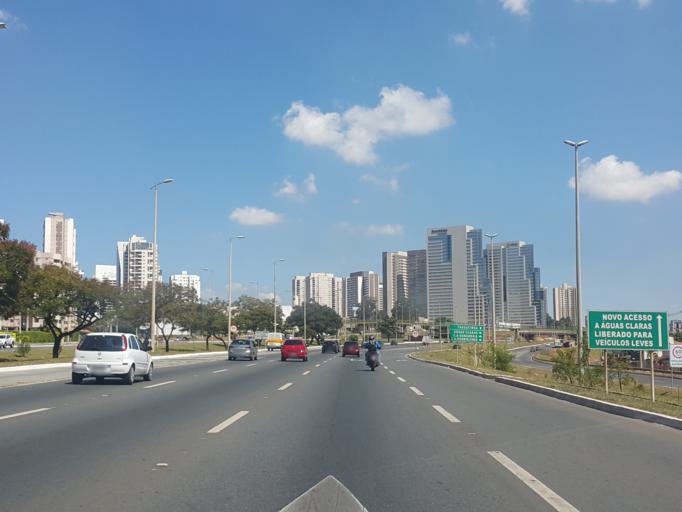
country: BR
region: Federal District
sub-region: Brasilia
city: Brasilia
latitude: -15.8281
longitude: -48.0327
